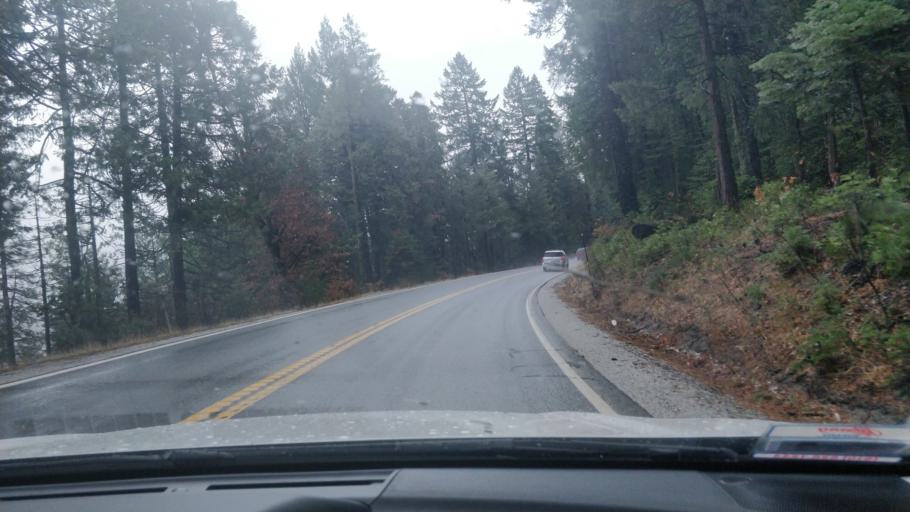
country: US
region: California
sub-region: Nevada County
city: Nevada City
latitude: 39.3216
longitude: -120.8215
